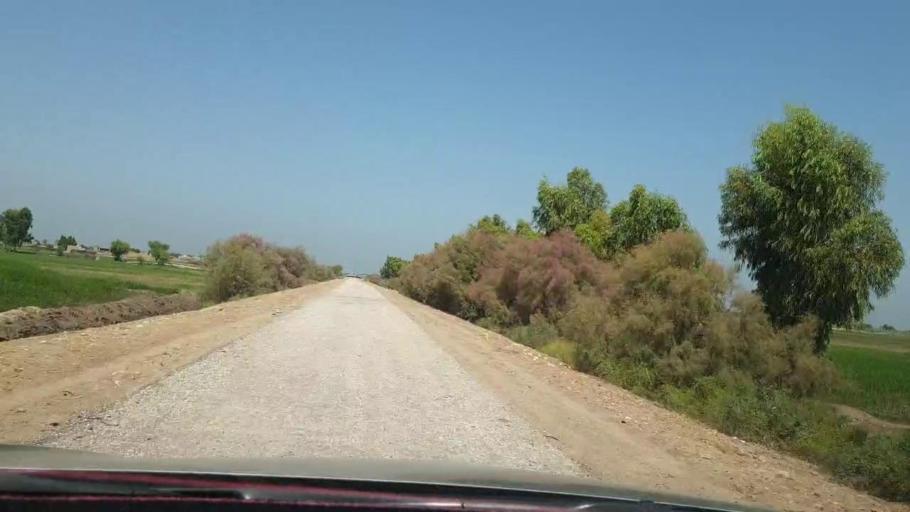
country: PK
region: Sindh
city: Warah
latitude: 27.5385
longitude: 67.7412
